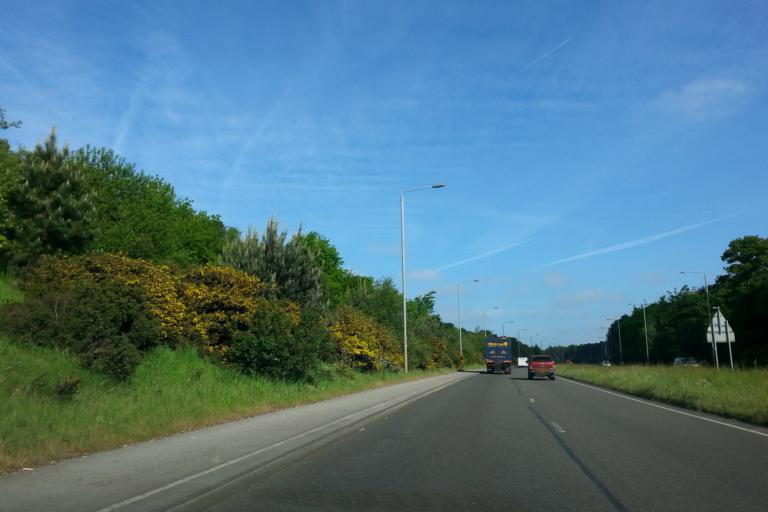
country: GB
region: England
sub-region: Nottinghamshire
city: Rainworth
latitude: 53.1241
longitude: -1.1211
